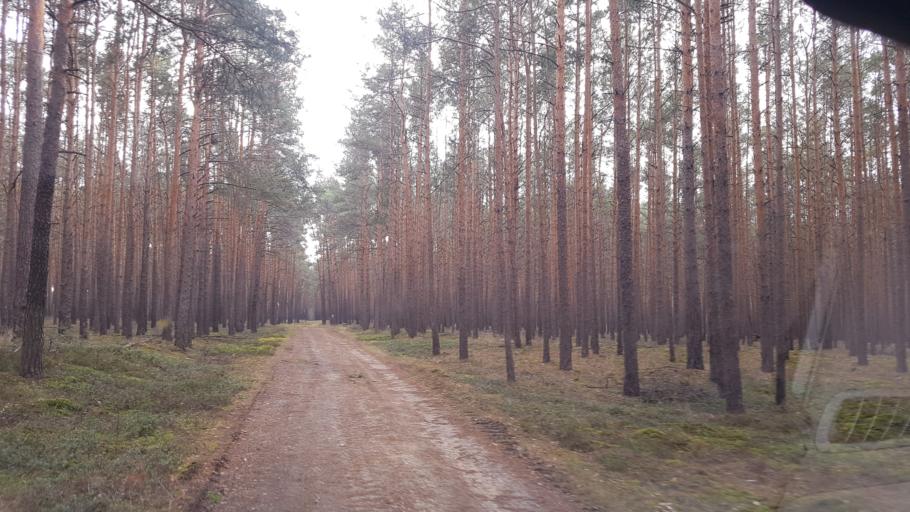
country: DE
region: Brandenburg
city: Schonborn
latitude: 51.6582
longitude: 13.4709
